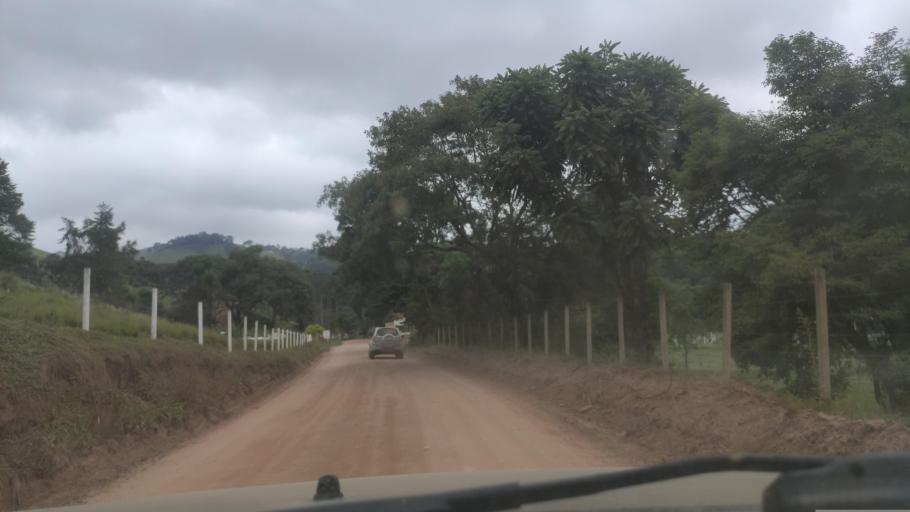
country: BR
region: Minas Gerais
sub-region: Paraisopolis
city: Paraisopolis
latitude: -22.6602
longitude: -45.8929
